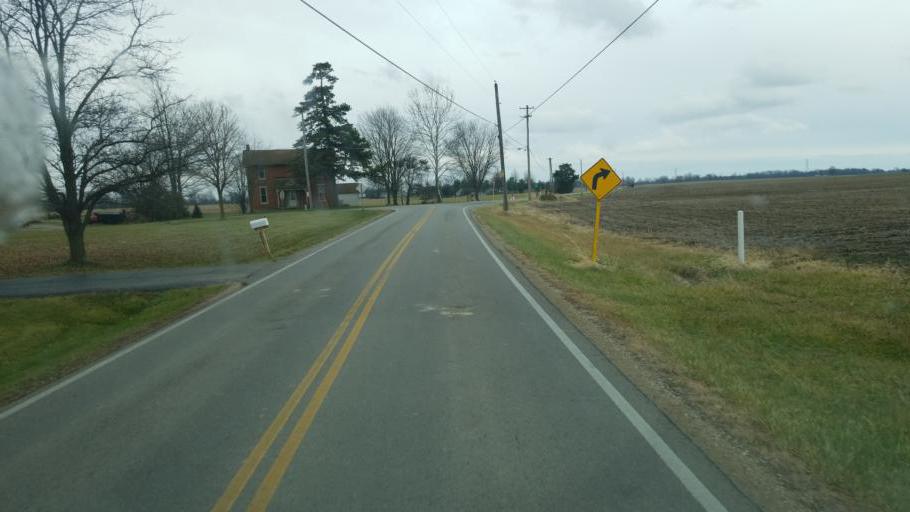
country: US
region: Ohio
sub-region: Delaware County
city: Delaware
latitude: 40.2801
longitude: -83.0330
